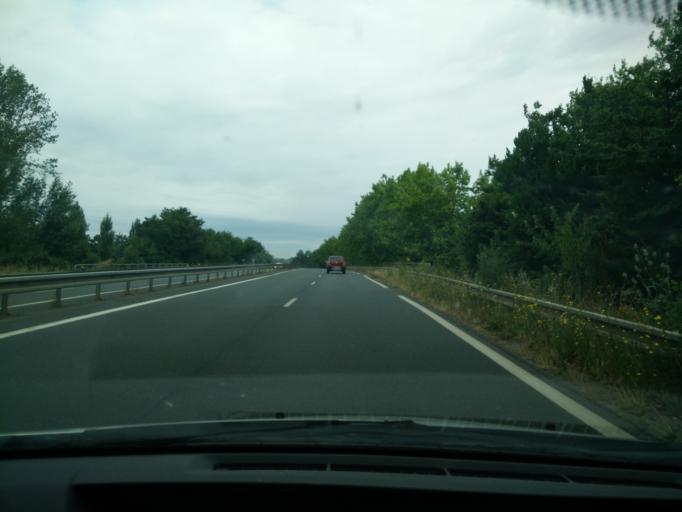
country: FR
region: Pays de la Loire
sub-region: Departement de Maine-et-Loire
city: Brissac-Quince
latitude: 47.3508
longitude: -0.4378
